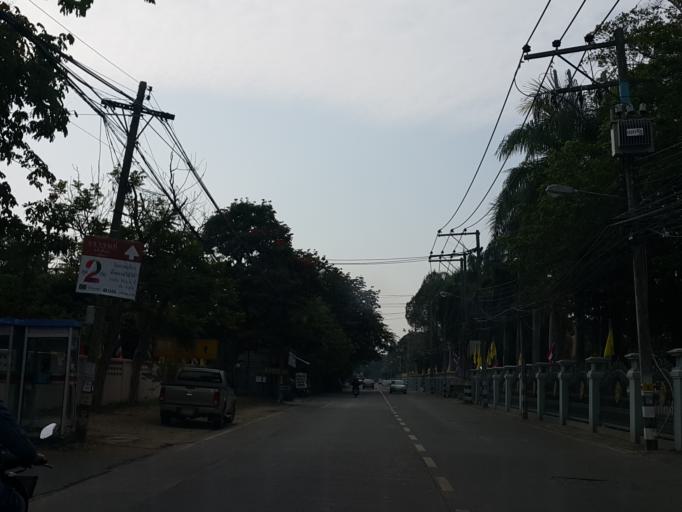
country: TH
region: Chiang Mai
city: Chiang Mai
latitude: 18.7913
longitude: 99.0179
